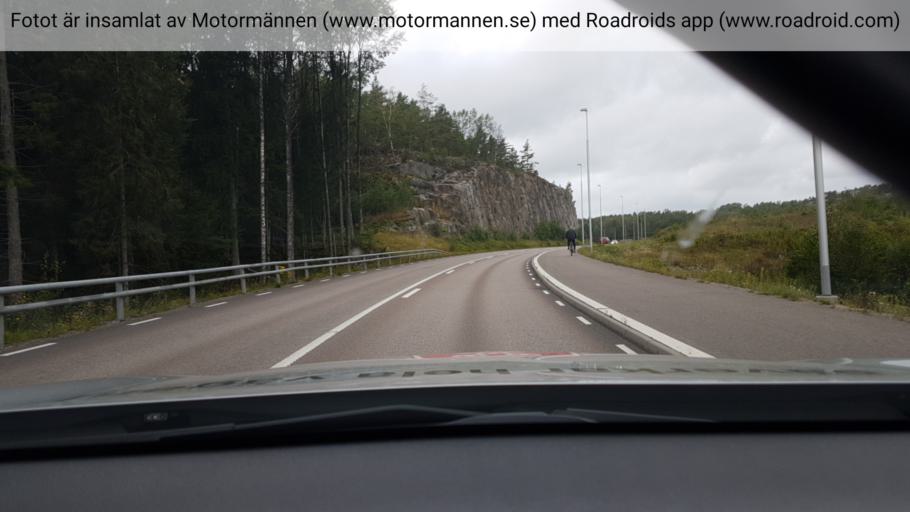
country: SE
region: Vaestra Goetaland
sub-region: Stromstads Kommun
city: Stroemstad
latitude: 58.9340
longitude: 11.2391
